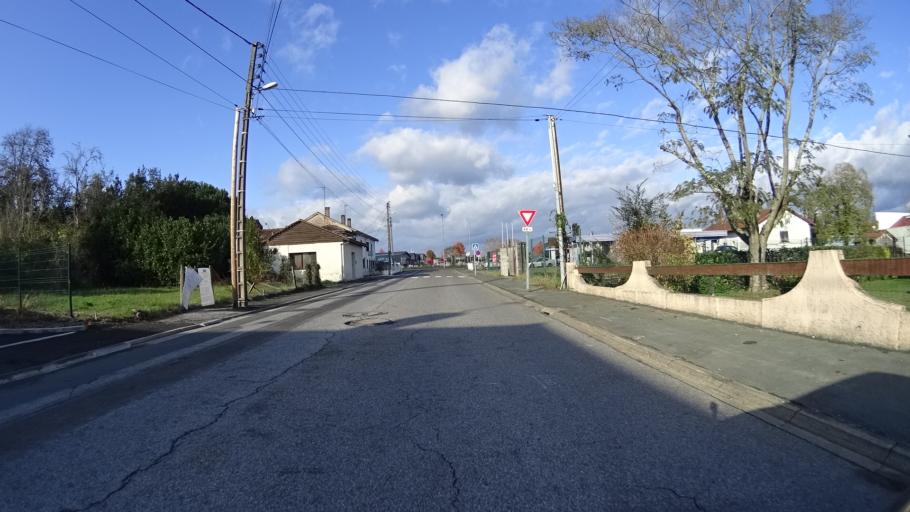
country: FR
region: Aquitaine
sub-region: Departement des Landes
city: Saint-Paul-les-Dax
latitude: 43.7264
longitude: -1.0837
